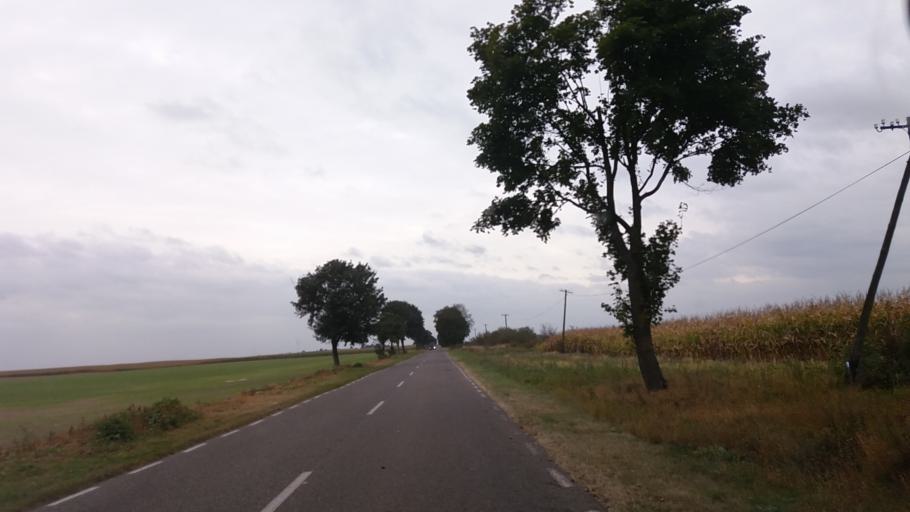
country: PL
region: Lubusz
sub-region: Powiat strzelecko-drezdenecki
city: Strzelce Krajenskie
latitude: 52.9531
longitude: 15.5714
